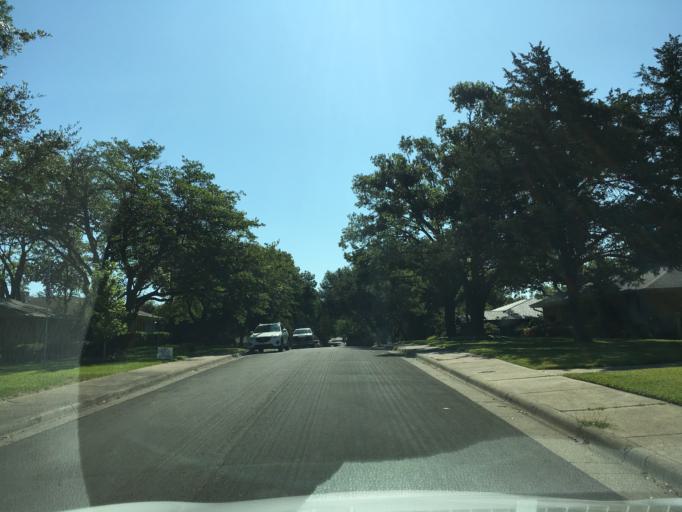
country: US
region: Texas
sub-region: Dallas County
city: Garland
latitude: 32.8616
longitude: -96.6987
